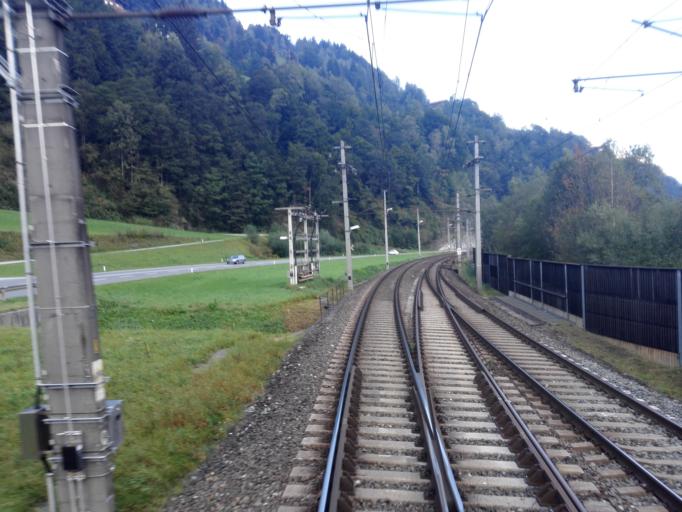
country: AT
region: Salzburg
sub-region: Politischer Bezirk Sankt Johann im Pongau
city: Bischofshofen
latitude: 47.3837
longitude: 13.2110
